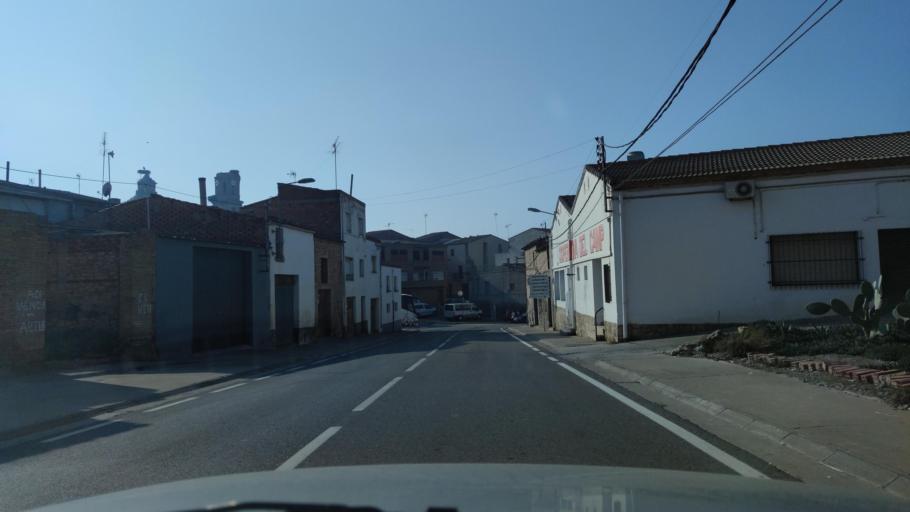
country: ES
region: Catalonia
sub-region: Provincia de Lleida
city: la Granja d'Escarp
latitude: 41.4600
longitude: 0.3601
